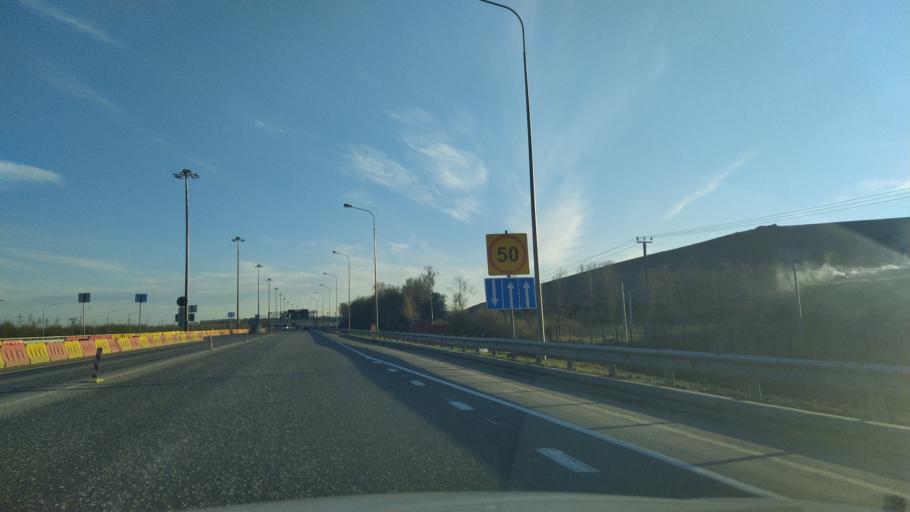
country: RU
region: St.-Petersburg
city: Levashovo
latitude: 60.0735
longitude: 30.1782
